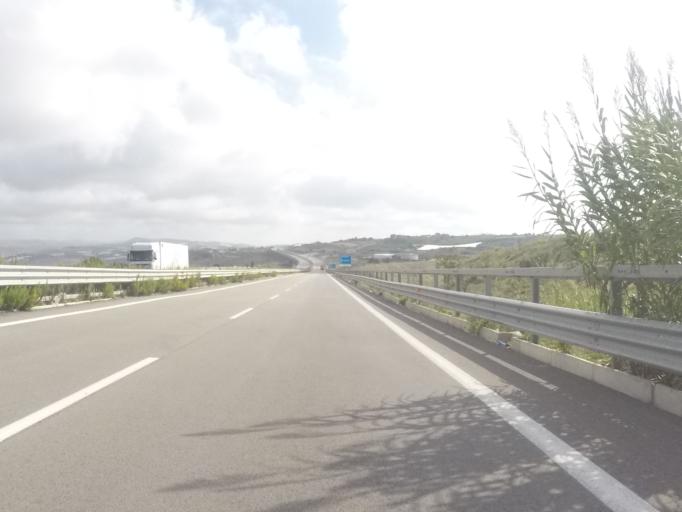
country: IT
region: Sicily
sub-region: Agrigento
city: Canicatti
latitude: 37.3790
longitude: 13.7988
